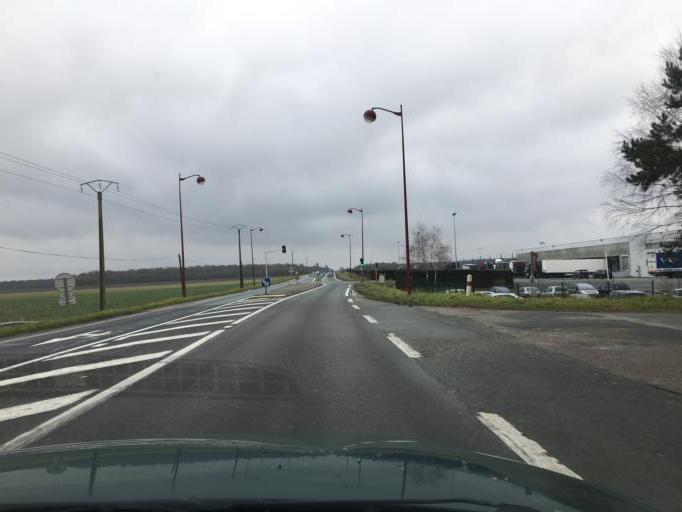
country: FR
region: Centre
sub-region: Departement du Loiret
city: Chevilly
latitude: 47.9902
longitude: 1.8821
